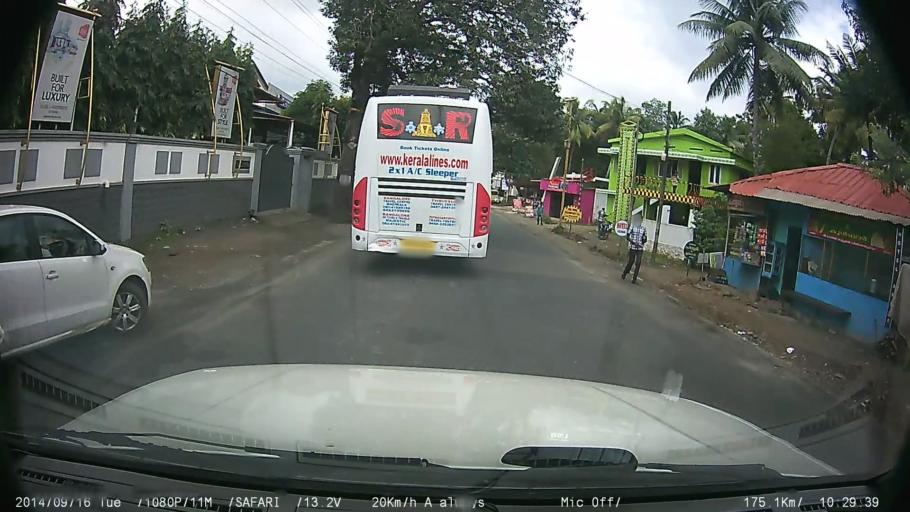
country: IN
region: Kerala
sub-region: Kottayam
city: Kottayam
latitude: 9.6351
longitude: 76.5443
